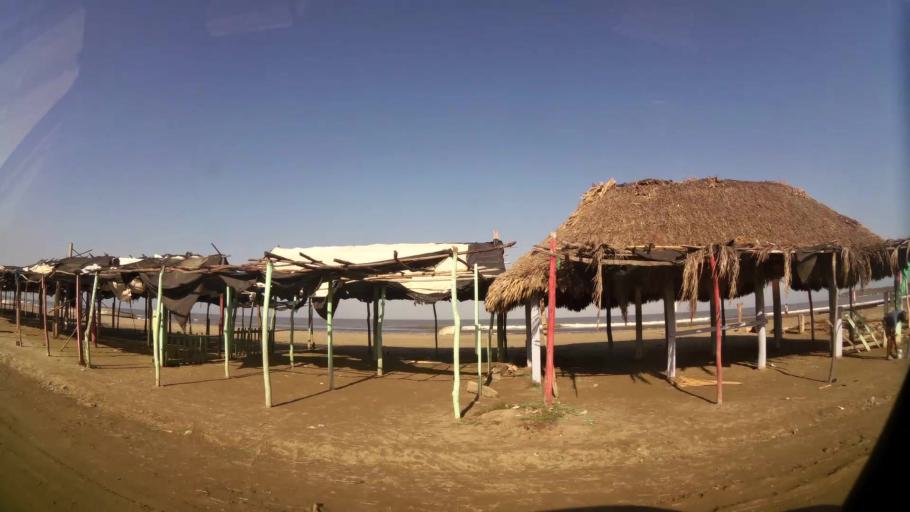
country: CO
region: Bolivar
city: Cartagena
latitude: 10.4820
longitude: -75.4933
